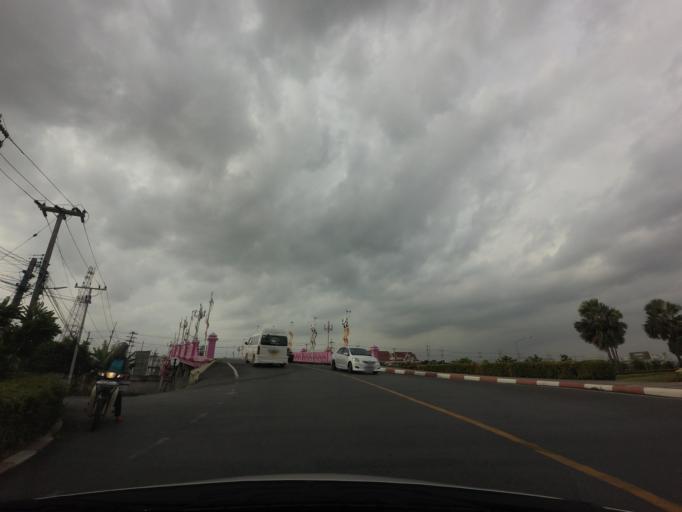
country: TH
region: Pathum Thani
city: Thanyaburi
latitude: 13.9964
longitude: 100.6749
